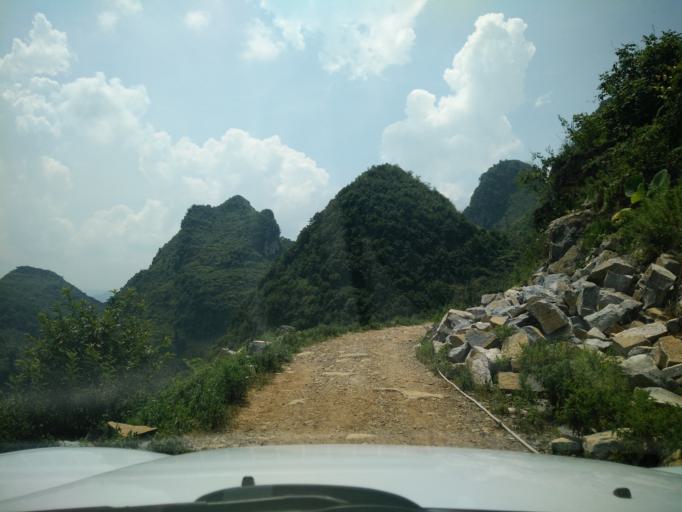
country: CN
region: Guangxi Zhuangzu Zizhiqu
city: Xinzhou
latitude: 25.0022
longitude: 105.6976
